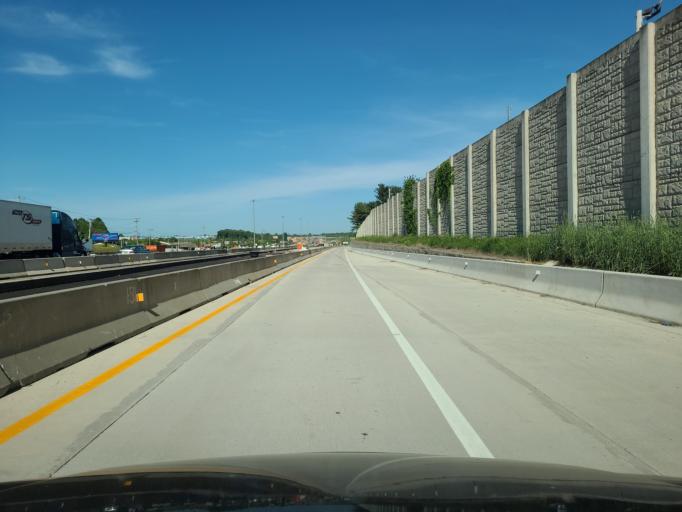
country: US
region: North Carolina
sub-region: Iredell County
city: Statesville
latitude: 35.8056
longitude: -80.8835
